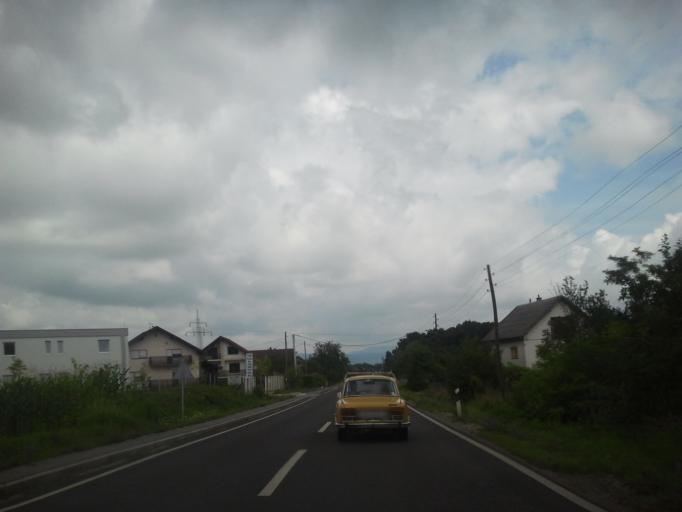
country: HR
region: Zagrebacka
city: Kerestinec
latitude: 45.7411
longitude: 15.8006
